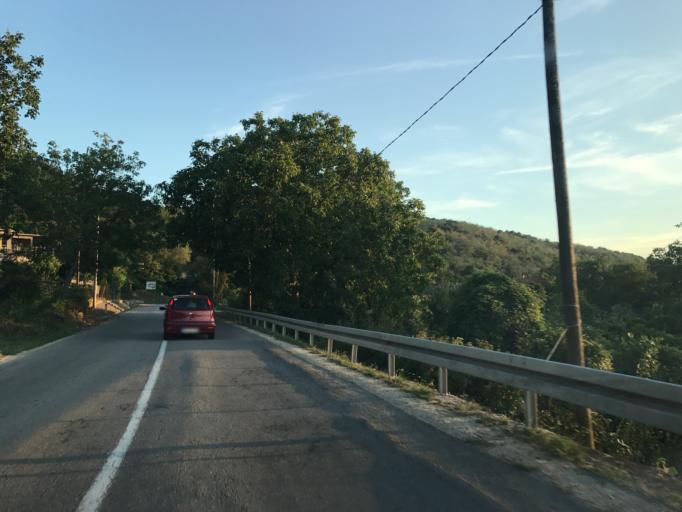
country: RS
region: Central Serbia
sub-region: Branicevski Okrug
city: Golubac
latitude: 44.6565
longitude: 21.6556
